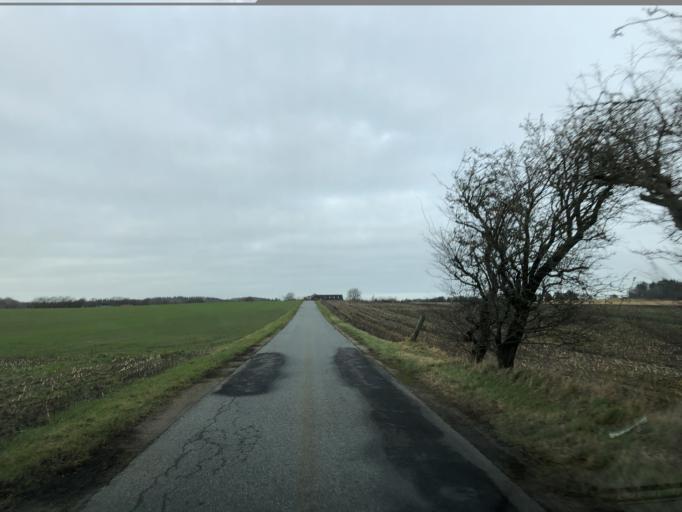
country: DK
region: Central Jutland
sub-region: Viborg Kommune
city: Stoholm
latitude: 56.4509
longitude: 9.1279
